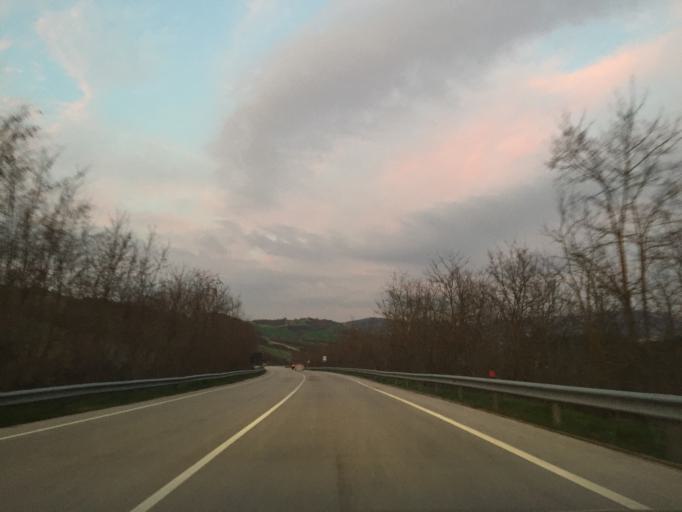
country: IT
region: Molise
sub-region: Provincia di Campobasso
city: Gambatesa
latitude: 41.5229
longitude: 14.9493
